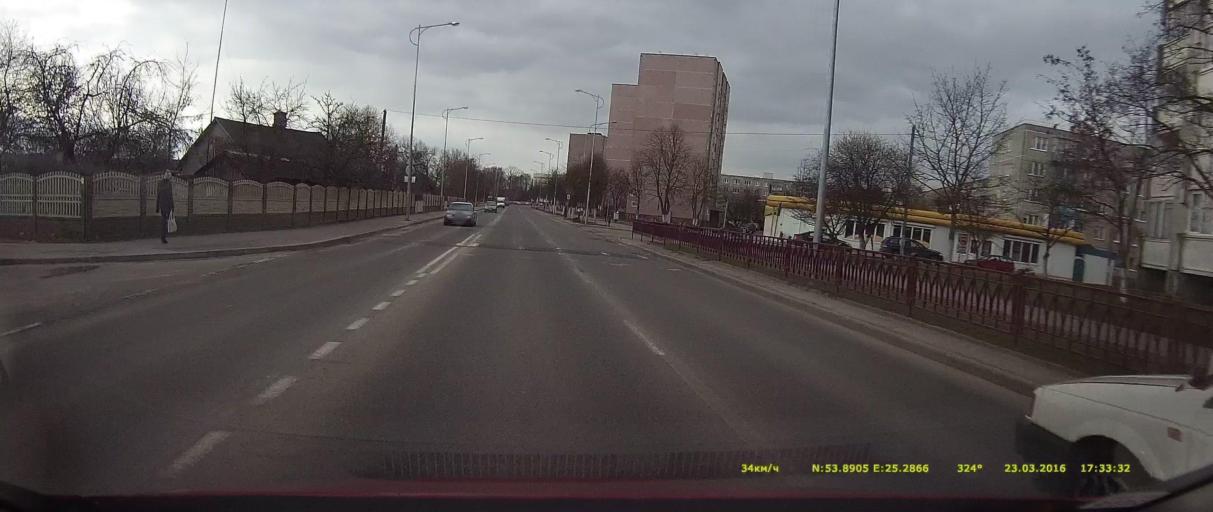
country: BY
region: Grodnenskaya
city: Lida
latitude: 53.8906
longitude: 25.2865
